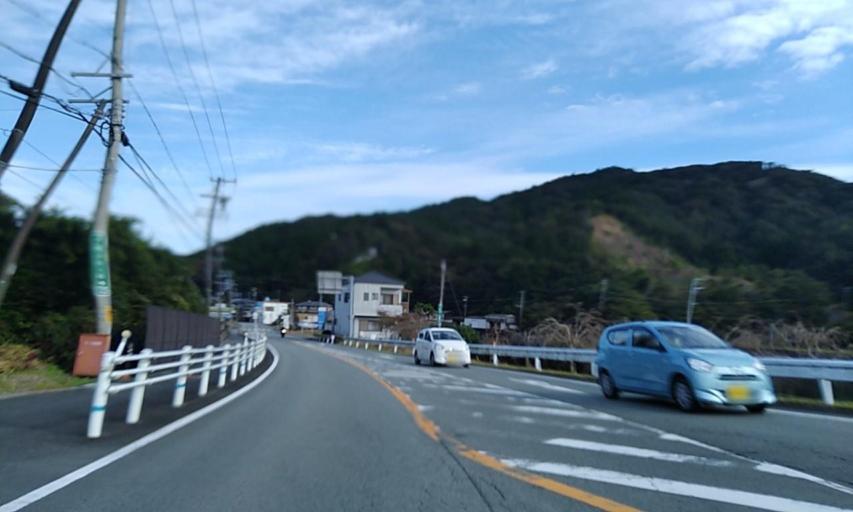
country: JP
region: Mie
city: Ise
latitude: 34.3432
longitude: 136.7272
